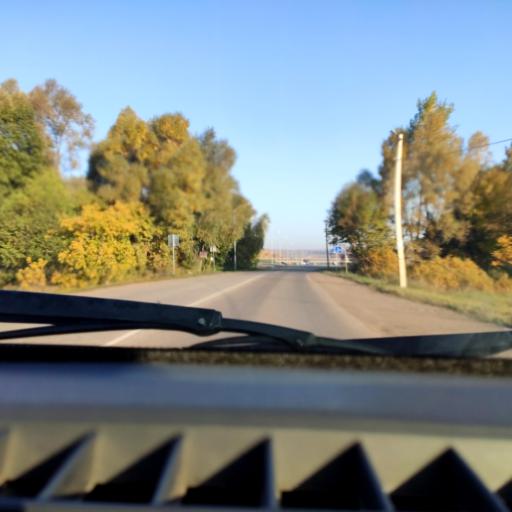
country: RU
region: Bashkortostan
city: Avdon
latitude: 54.6611
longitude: 55.7365
